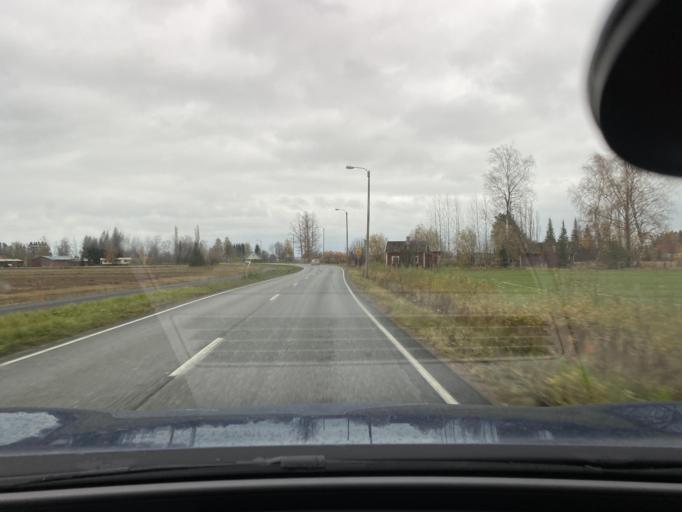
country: FI
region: Satakunta
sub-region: Rauma
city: Saekylae
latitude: 61.0619
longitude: 22.4977
